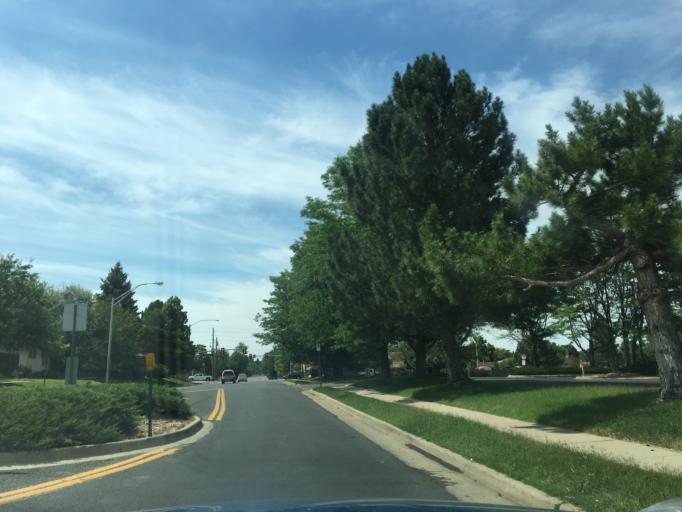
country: US
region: Colorado
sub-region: Adams County
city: Aurora
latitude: 39.7124
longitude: -104.8548
